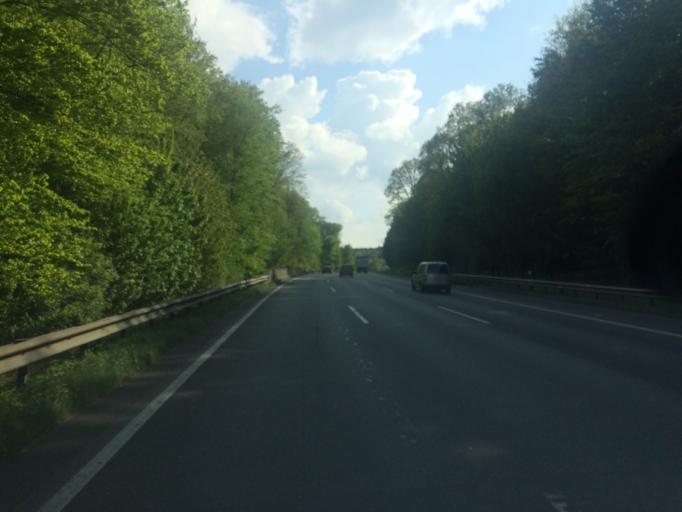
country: DE
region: North Rhine-Westphalia
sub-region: Regierungsbezirk Detmold
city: Bad Salzuflen
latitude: 52.1152
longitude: 8.7370
